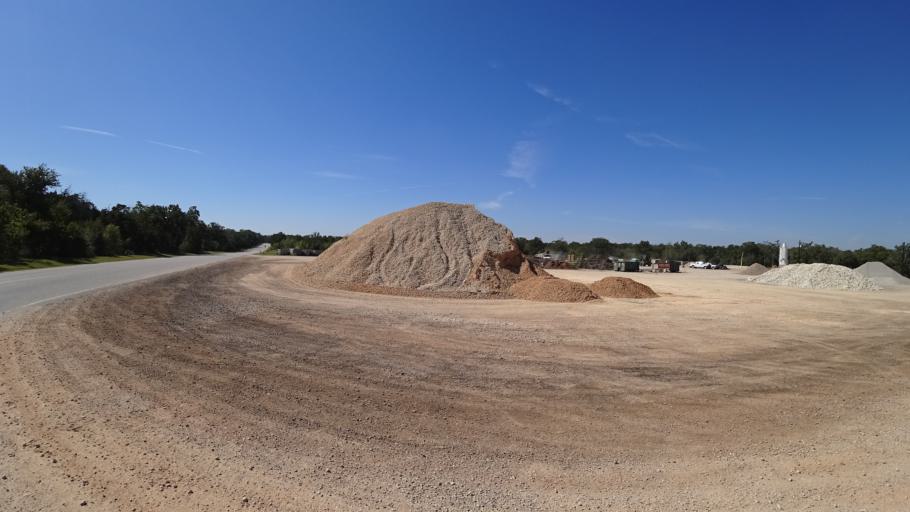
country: US
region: Texas
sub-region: Travis County
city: Hornsby Bend
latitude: 30.2744
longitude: -97.6075
